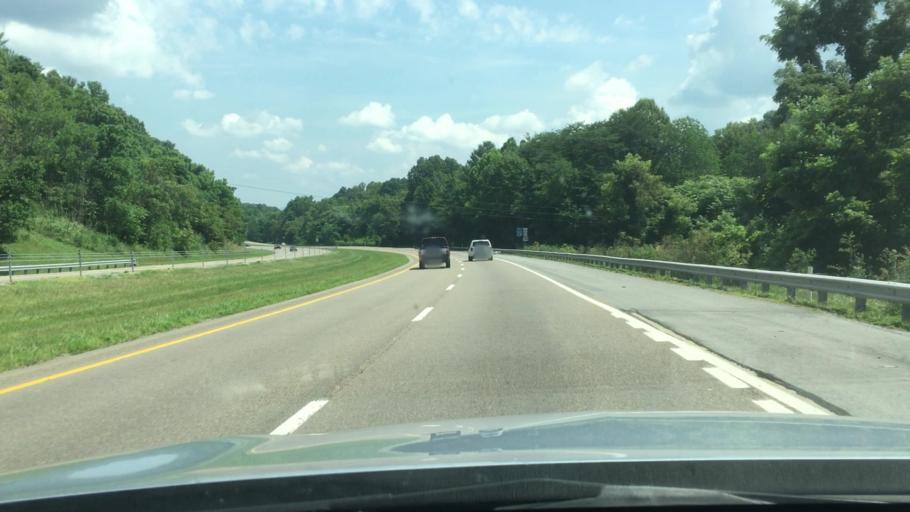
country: US
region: Tennessee
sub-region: Unicoi County
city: Unicoi
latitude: 36.2117
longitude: -82.3480
